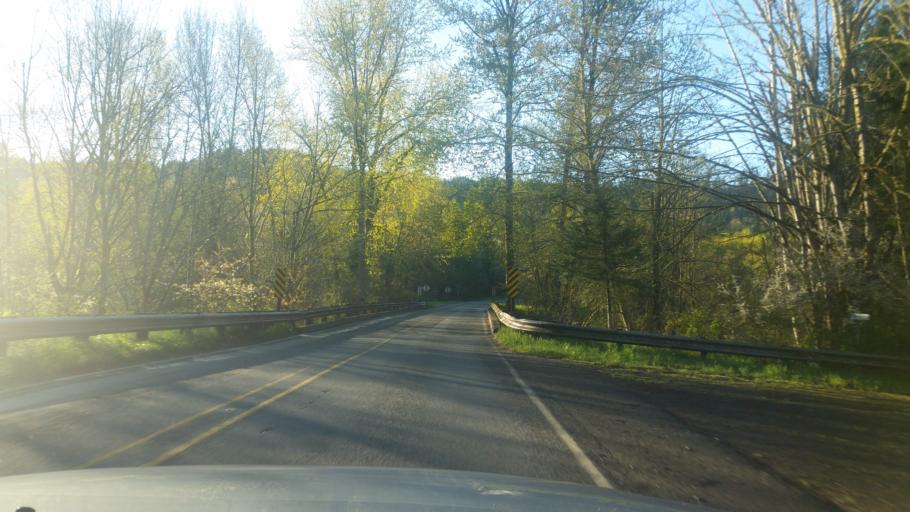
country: US
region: Washington
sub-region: Pierce County
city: Eatonville
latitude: 46.8638
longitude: -122.2529
